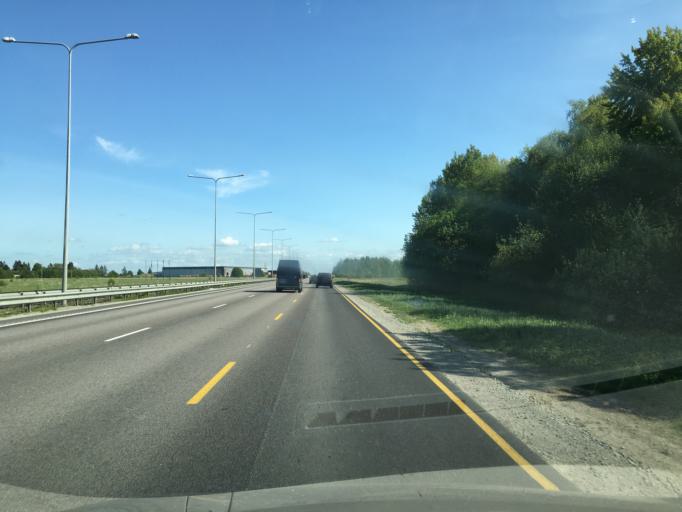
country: EE
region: Harju
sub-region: Rae vald
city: Jueri
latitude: 59.3712
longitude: 24.8545
